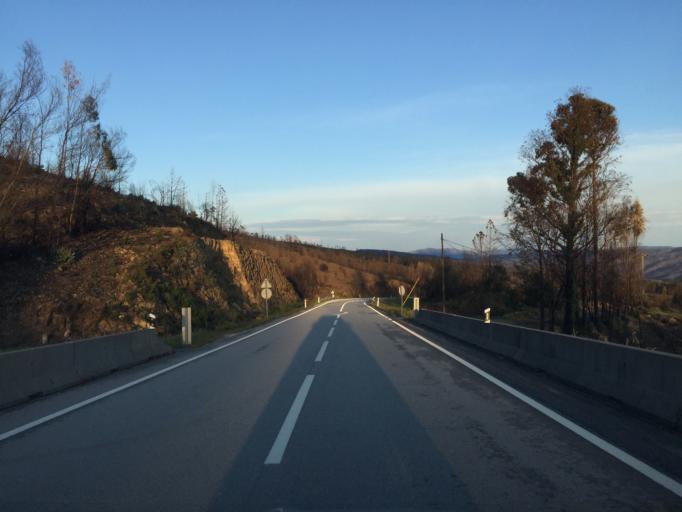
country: PT
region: Coimbra
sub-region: Pampilhosa da Serra
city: Pampilhosa da Serra
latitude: 40.0817
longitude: -7.9868
